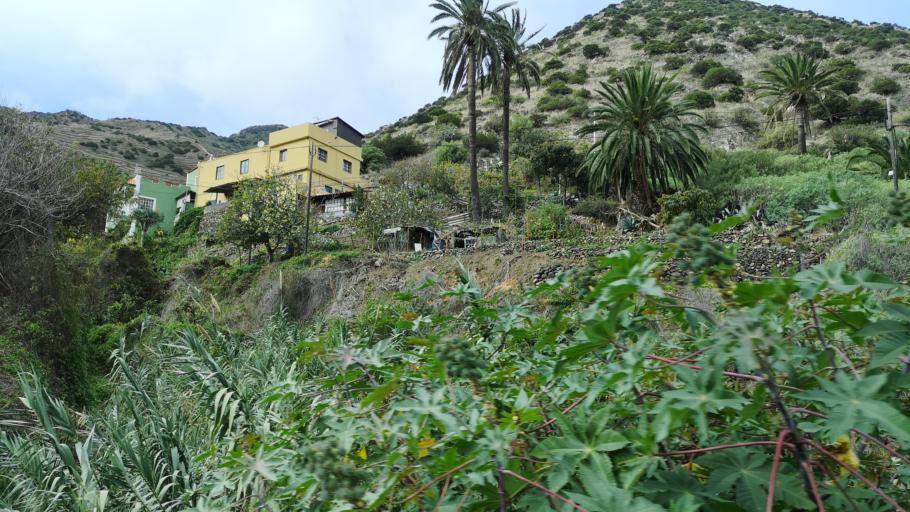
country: ES
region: Canary Islands
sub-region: Provincia de Santa Cruz de Tenerife
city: Vallehermosa
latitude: 28.1861
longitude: -17.2641
